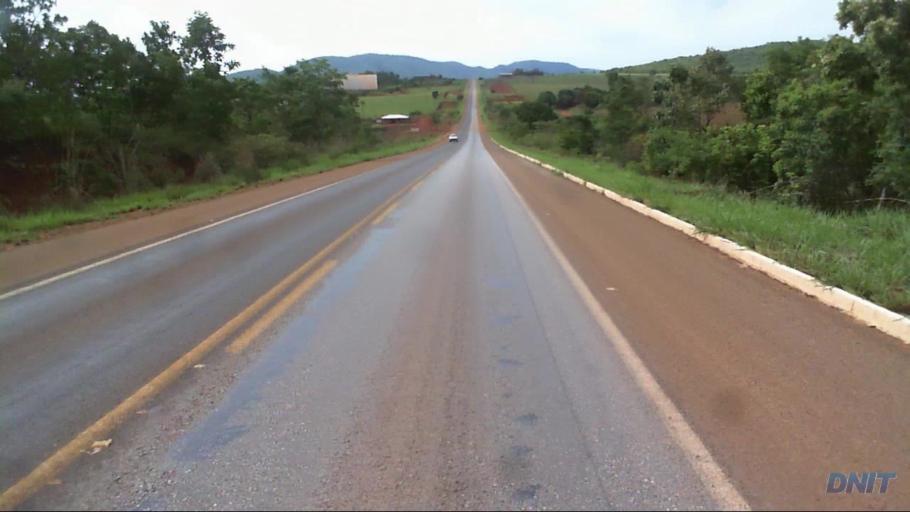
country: BR
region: Goias
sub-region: Barro Alto
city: Barro Alto
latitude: -14.9538
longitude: -48.9323
